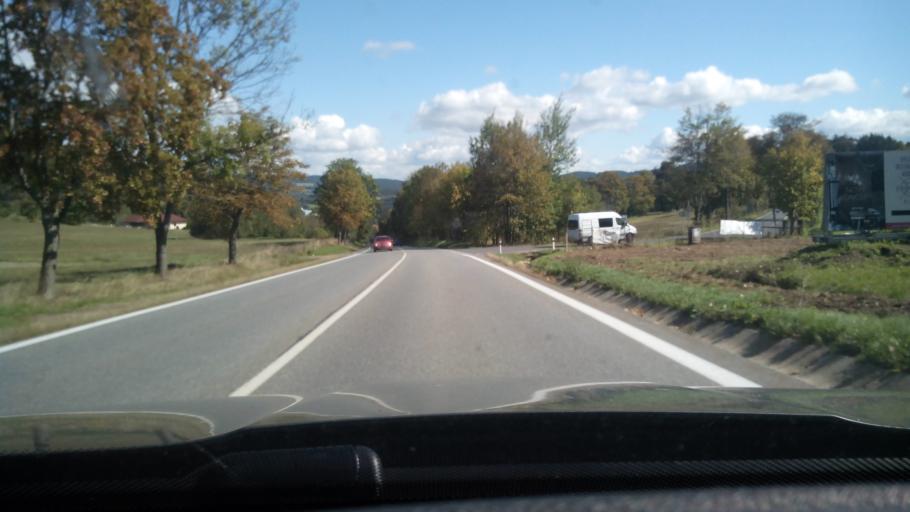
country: CZ
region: Jihocesky
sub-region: Okres Prachatice
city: Vimperk
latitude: 49.0608
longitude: 13.7605
